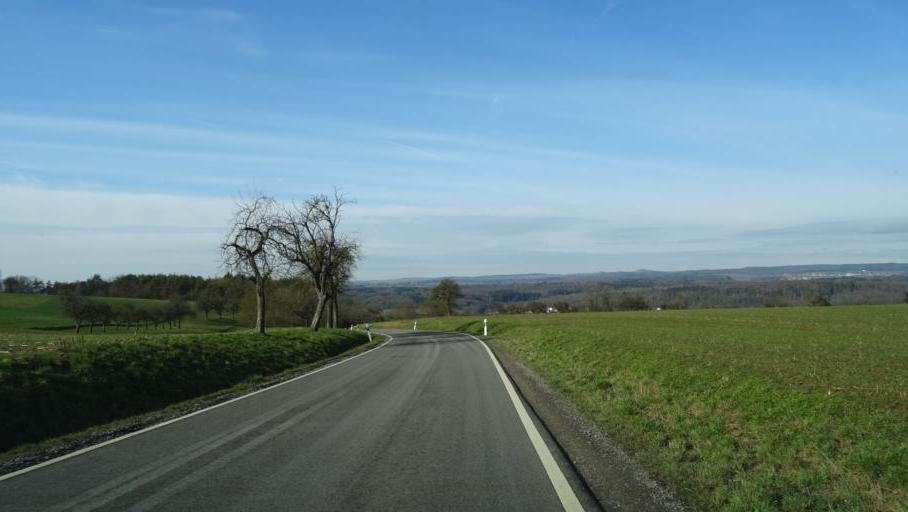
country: DE
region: Baden-Wuerttemberg
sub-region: Karlsruhe Region
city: Billigheim
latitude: 49.3787
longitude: 9.2059
